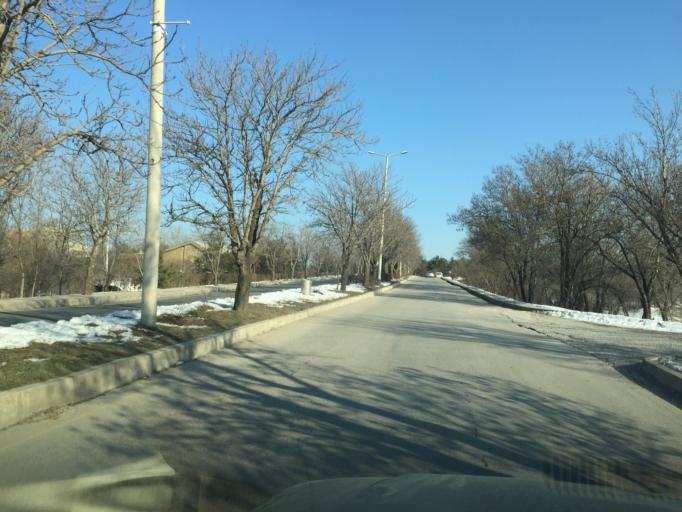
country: TR
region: Ankara
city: Ankara
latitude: 39.8996
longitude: 32.7784
